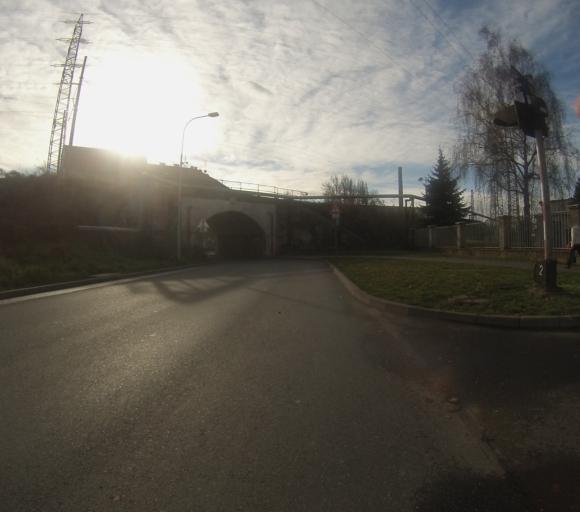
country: CZ
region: South Moravian
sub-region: Mesto Brno
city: Brno
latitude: 49.1948
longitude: 16.6226
